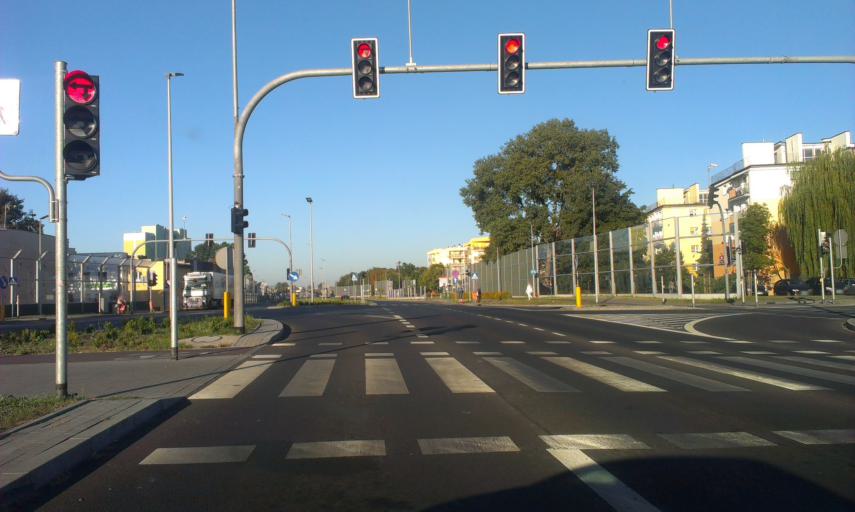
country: PL
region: Kujawsko-Pomorskie
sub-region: Torun
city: Torun
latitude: 53.0264
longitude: 18.6022
